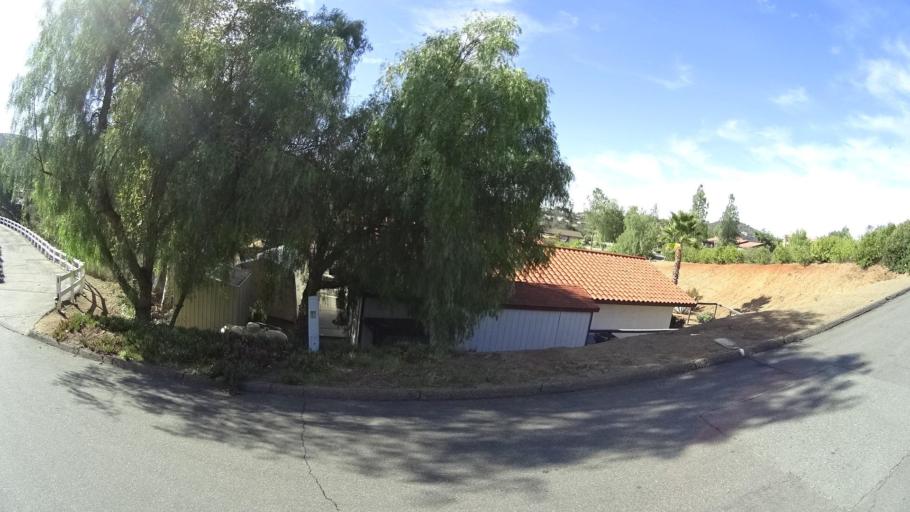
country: US
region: California
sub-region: San Diego County
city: Alpine
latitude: 32.8173
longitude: -116.7384
